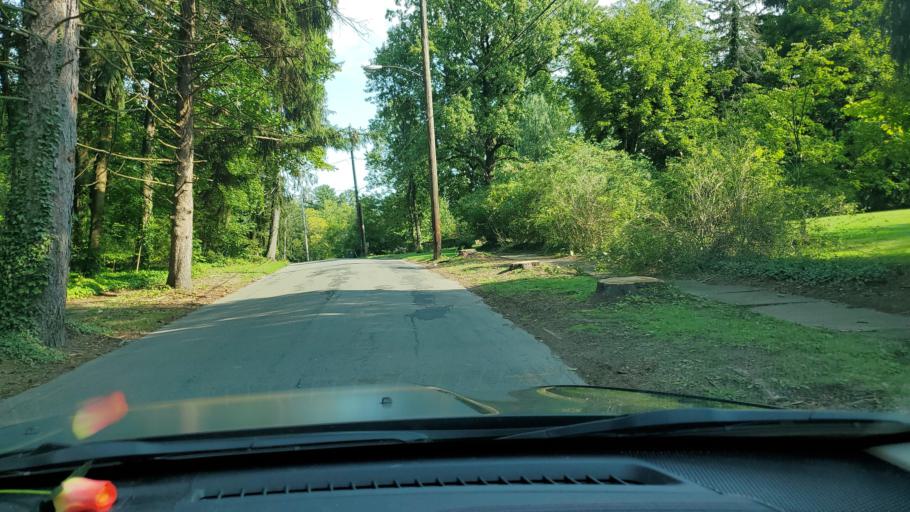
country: US
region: Ohio
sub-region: Mahoning County
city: Youngstown
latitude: 41.0829
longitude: -80.6776
